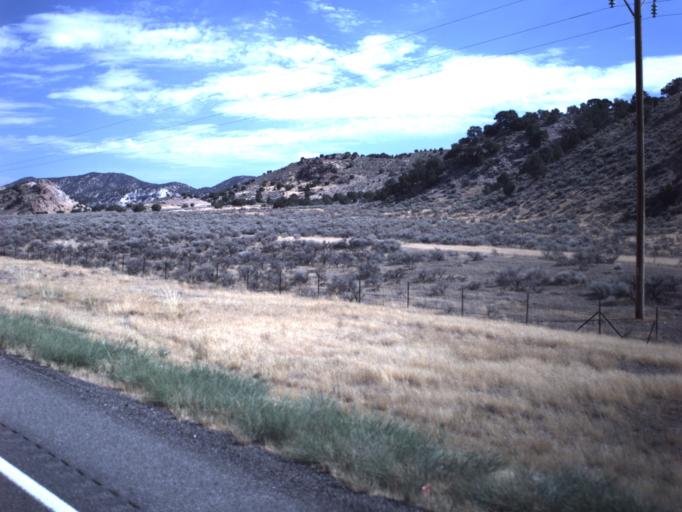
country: US
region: Utah
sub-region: Sanpete County
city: Gunnison
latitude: 39.3576
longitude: -111.9296
